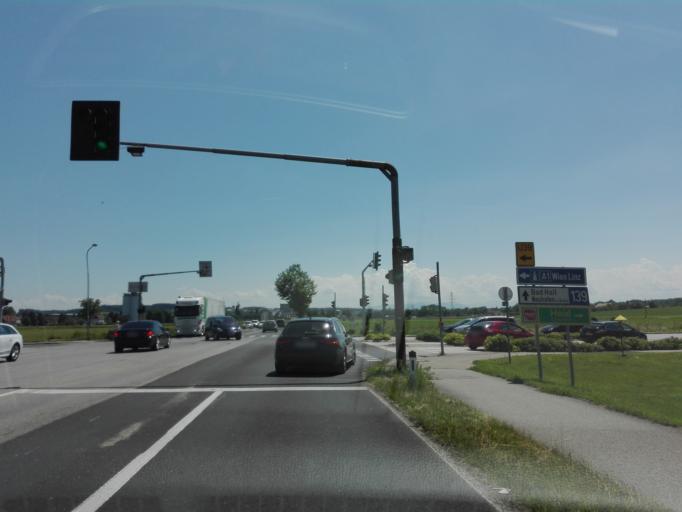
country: AT
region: Upper Austria
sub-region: Politischer Bezirk Linz-Land
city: Traun
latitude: 48.1946
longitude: 14.2500
